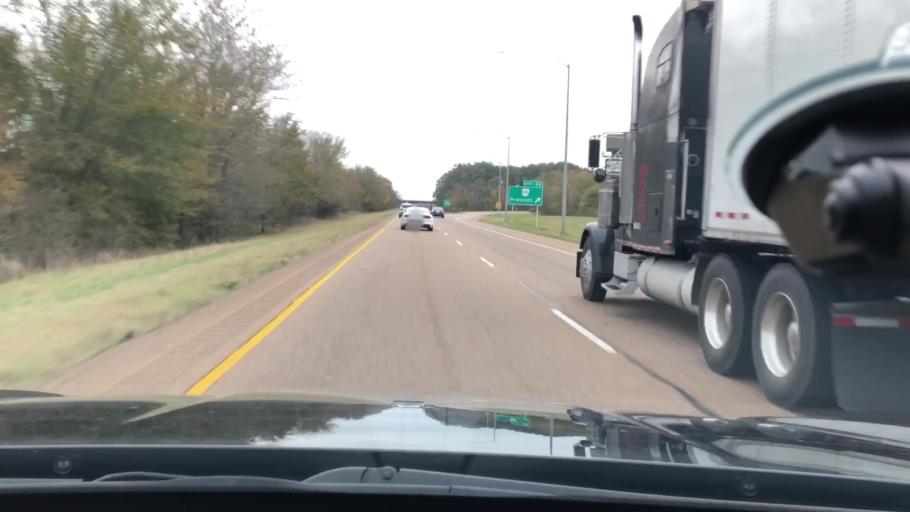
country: US
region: Arkansas
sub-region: Nevada County
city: Prescott
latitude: 33.8277
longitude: -93.3998
